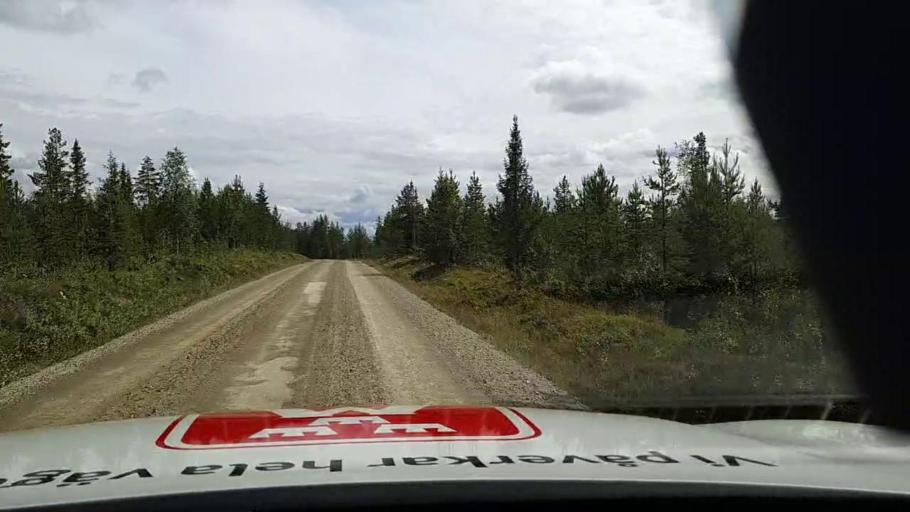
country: SE
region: Jaemtland
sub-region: Are Kommun
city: Jarpen
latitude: 62.5375
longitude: 13.4763
